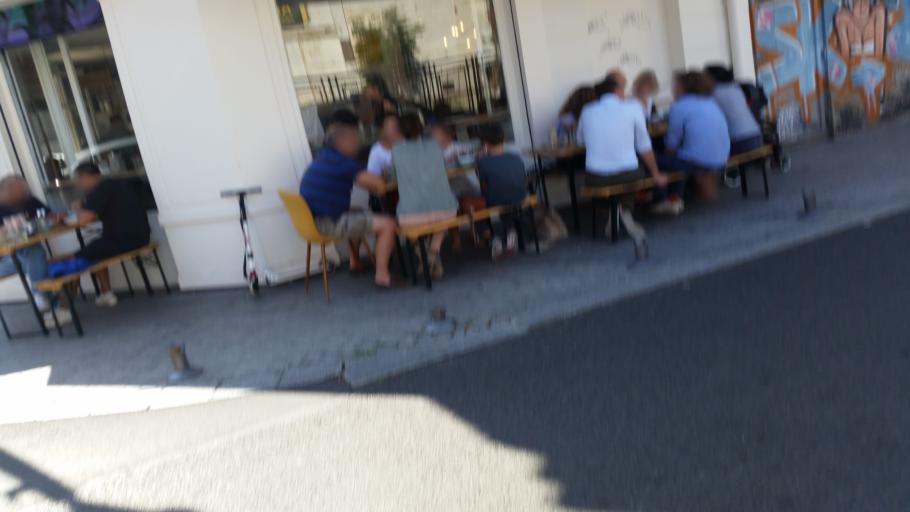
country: FR
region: Ile-de-France
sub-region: Paris
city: Saint-Ouen
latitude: 48.9033
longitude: 2.3366
